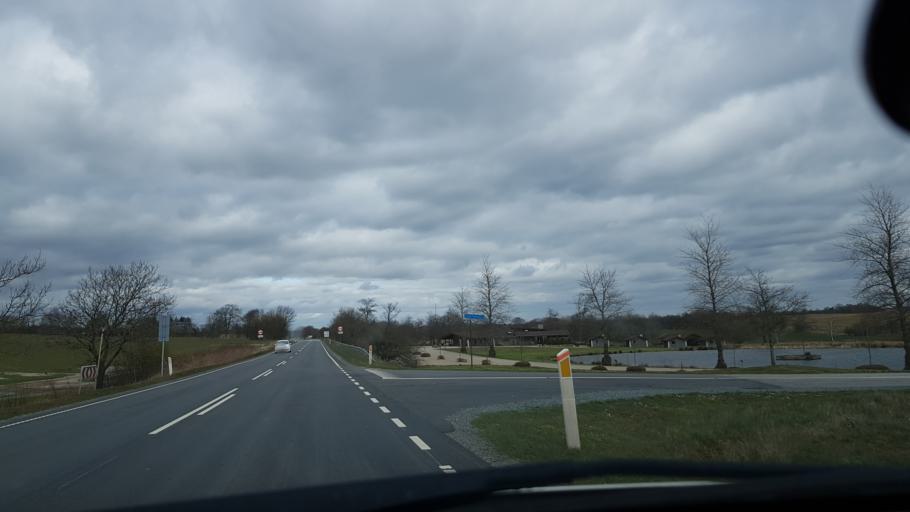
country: DK
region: South Denmark
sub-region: Vejen Kommune
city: Holsted
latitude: 55.4344
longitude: 8.9103
